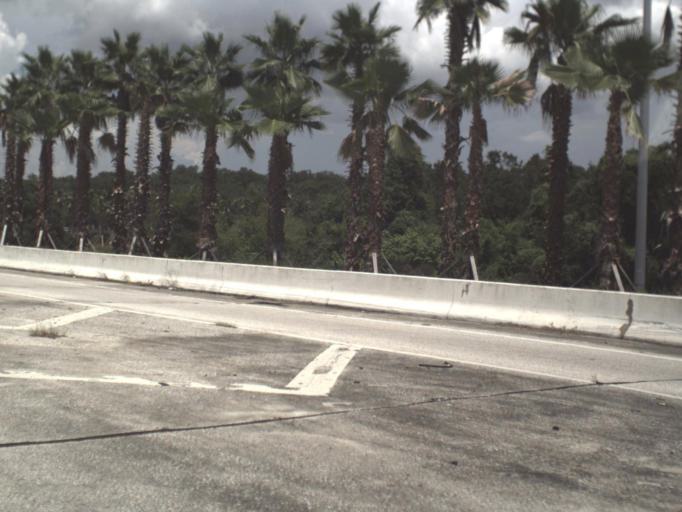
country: US
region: Florida
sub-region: Hillsborough County
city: Mango
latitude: 28.0046
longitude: -82.3271
